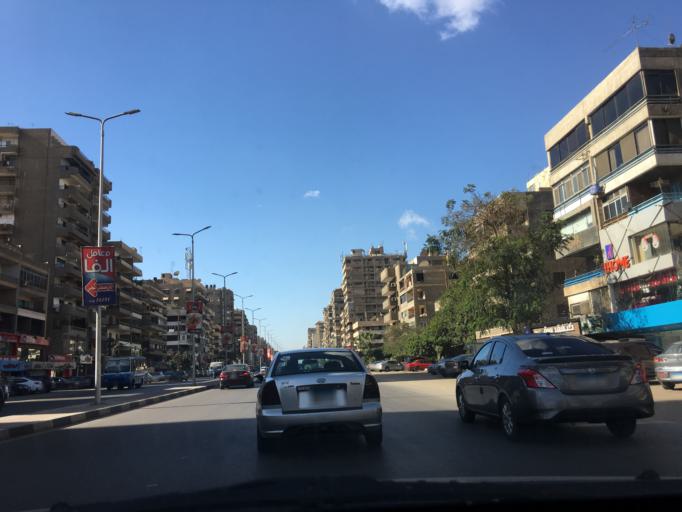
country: EG
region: Muhafazat al Qahirah
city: Cairo
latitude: 30.0545
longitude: 31.3441
